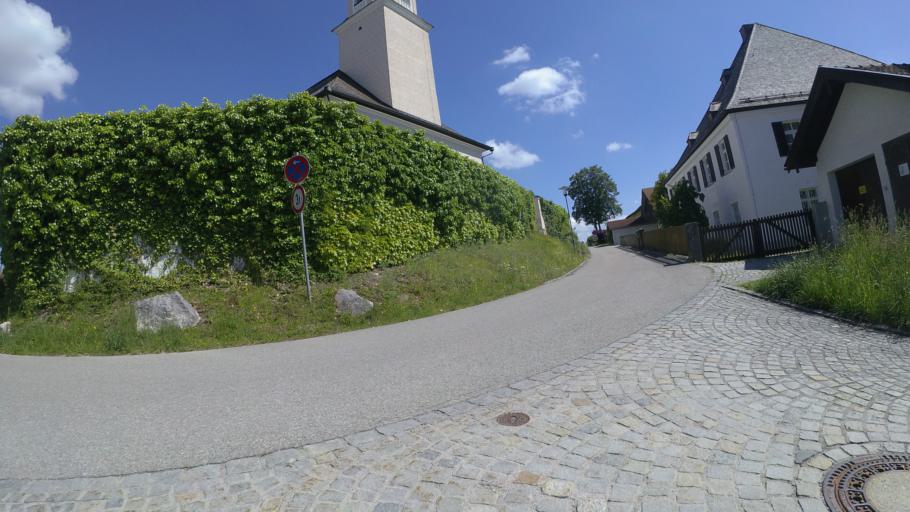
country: DE
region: Bavaria
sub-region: Upper Bavaria
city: Traunreut
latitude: 47.9394
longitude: 12.6015
